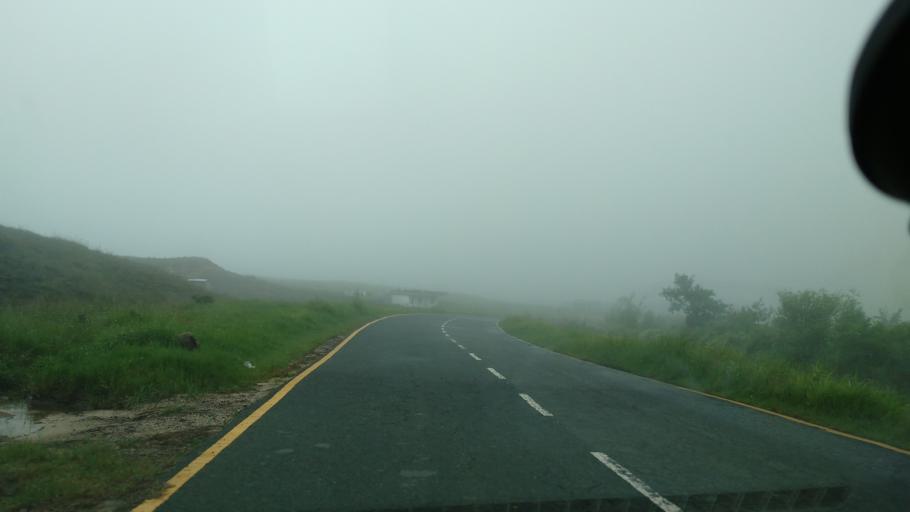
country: IN
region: Meghalaya
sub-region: East Khasi Hills
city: Cherrapunji
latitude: 25.3392
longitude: 91.7370
